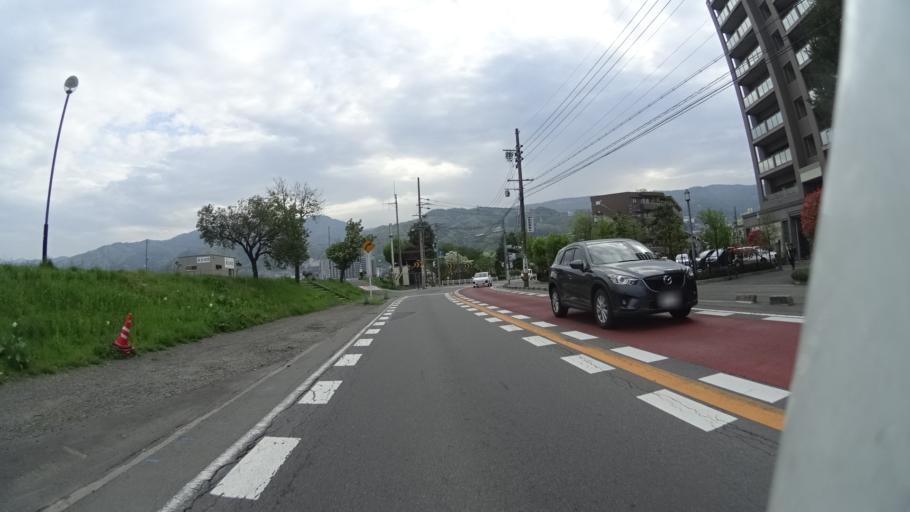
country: JP
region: Nagano
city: Suwa
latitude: 36.0462
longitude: 138.1091
